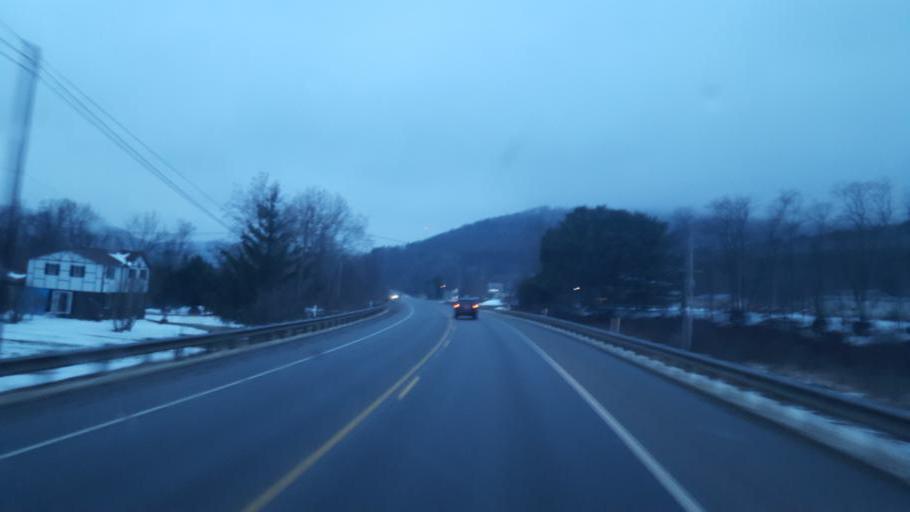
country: US
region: Pennsylvania
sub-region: McKean County
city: Port Allegany
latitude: 41.7928
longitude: -78.2144
